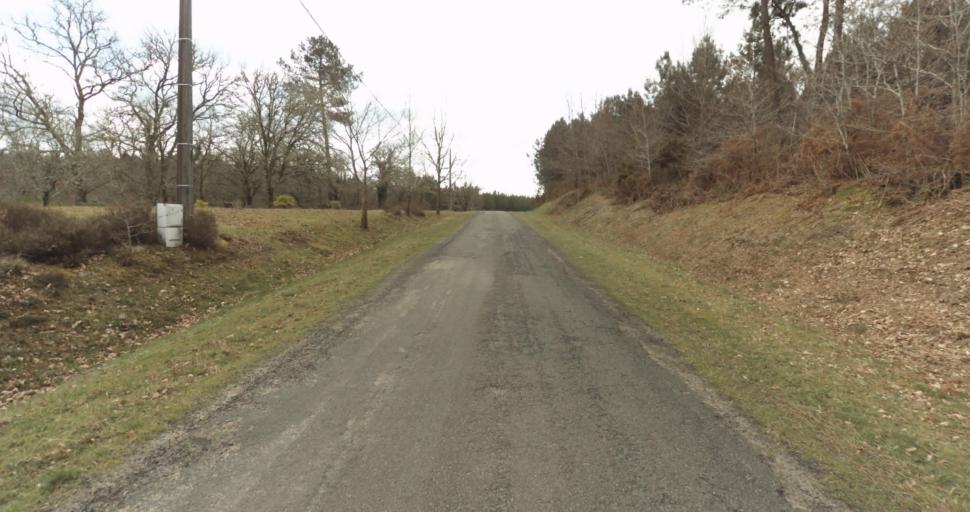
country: FR
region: Aquitaine
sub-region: Departement des Landes
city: Roquefort
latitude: 44.0663
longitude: -0.4314
